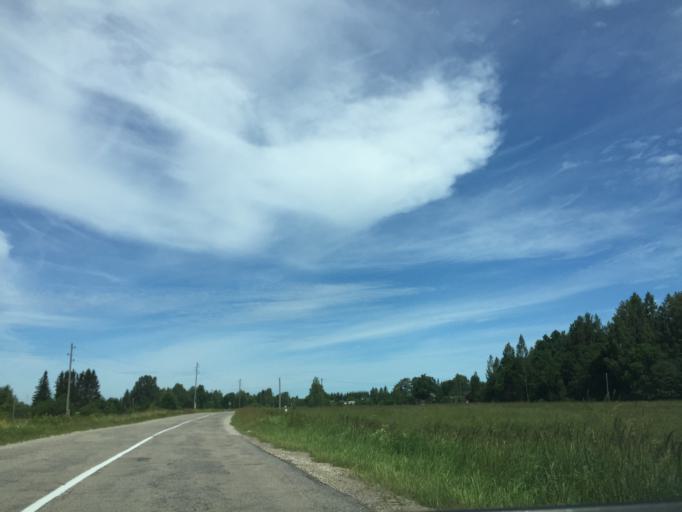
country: LV
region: Dundaga
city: Dundaga
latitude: 57.5220
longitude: 22.3331
